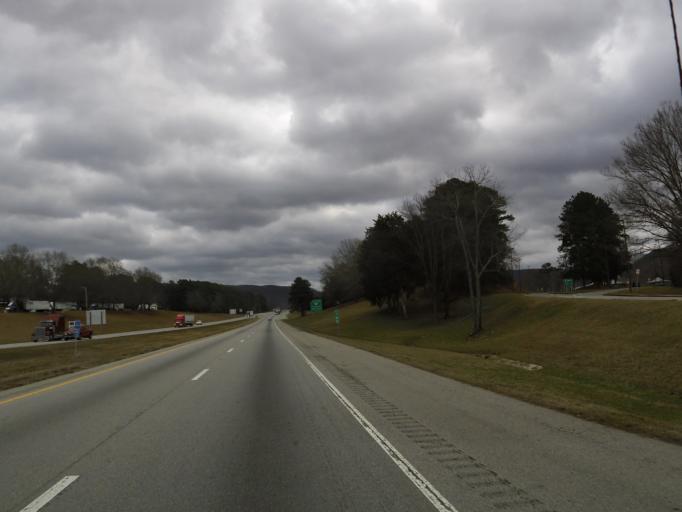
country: US
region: Tennessee
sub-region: Marion County
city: Jasper
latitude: 35.0260
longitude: -85.5608
